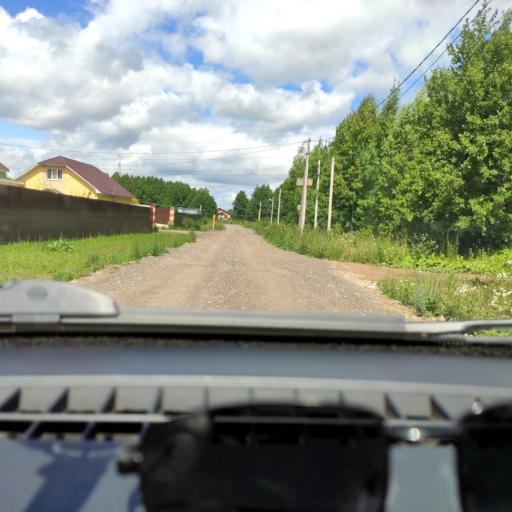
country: RU
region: Bashkortostan
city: Kabakovo
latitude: 54.6711
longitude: 56.0974
